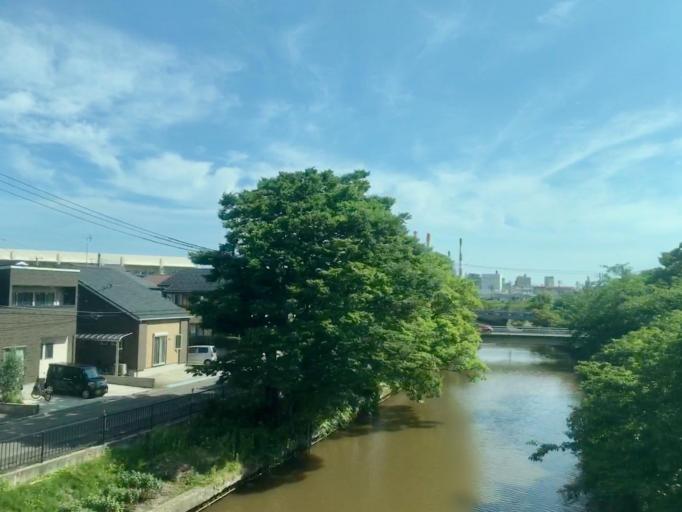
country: JP
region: Niigata
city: Niigata-shi
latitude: 37.9149
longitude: 139.0752
